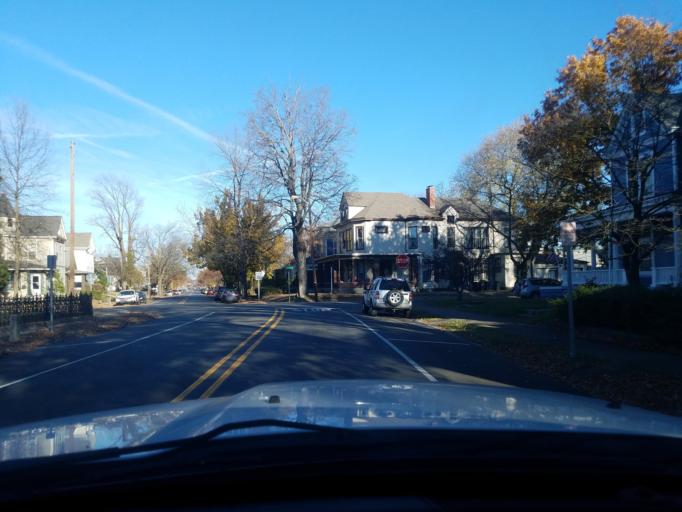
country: US
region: Indiana
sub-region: Floyd County
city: New Albany
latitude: 38.2899
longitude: -85.8148
